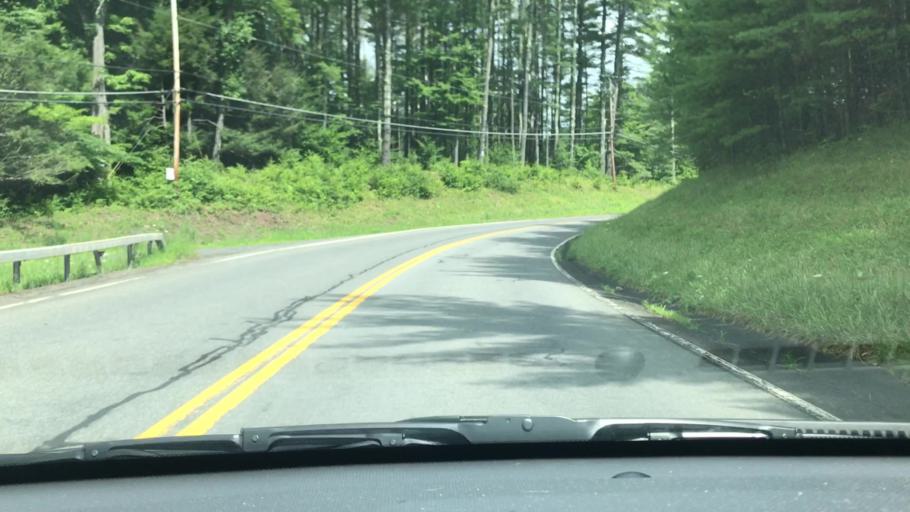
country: US
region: New York
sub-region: Ulster County
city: Shokan
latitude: 41.9932
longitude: -74.2782
